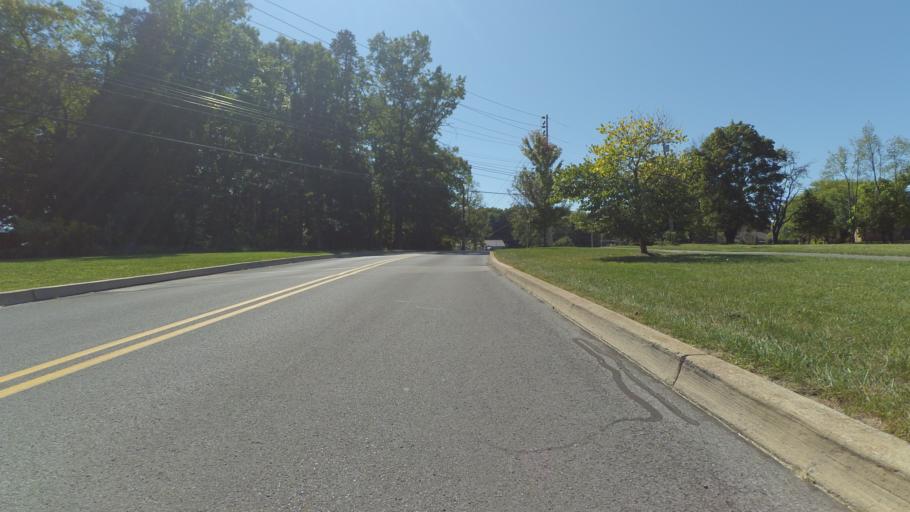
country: US
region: Pennsylvania
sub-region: Centre County
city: State College
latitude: 40.7747
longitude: -77.8884
